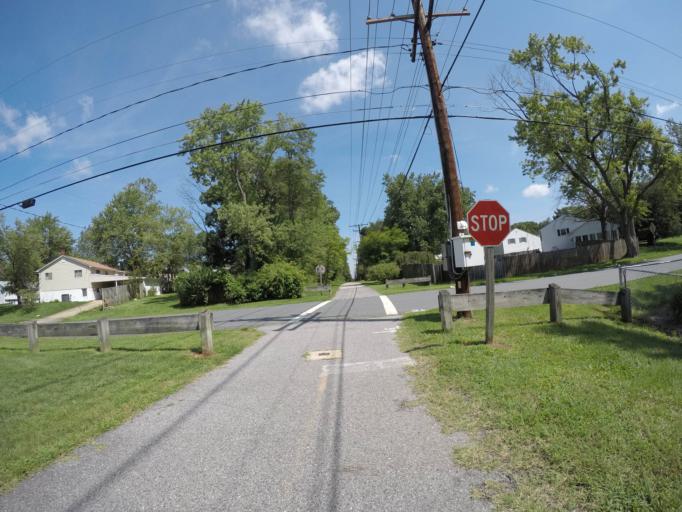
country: US
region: Maryland
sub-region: Anne Arundel County
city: Odenton
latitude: 39.0768
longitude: -76.7027
